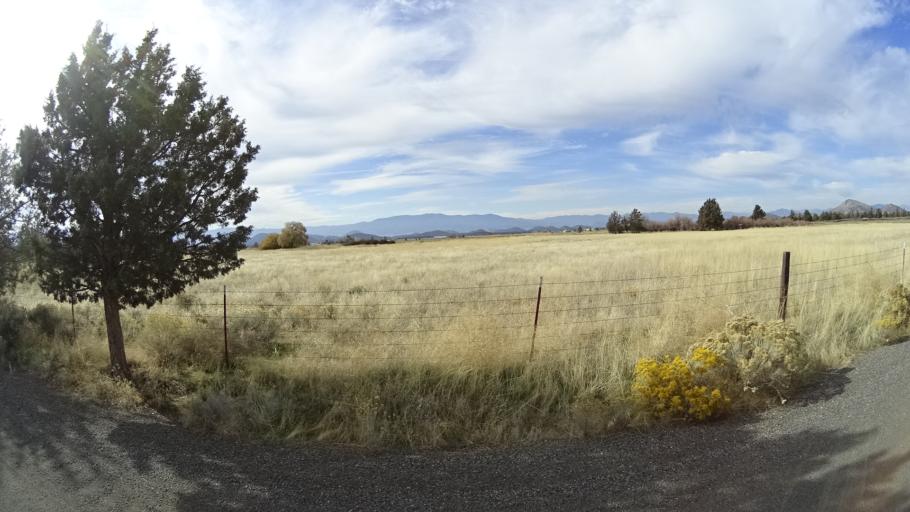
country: US
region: California
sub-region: Siskiyou County
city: Montague
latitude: 41.6187
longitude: -122.3801
